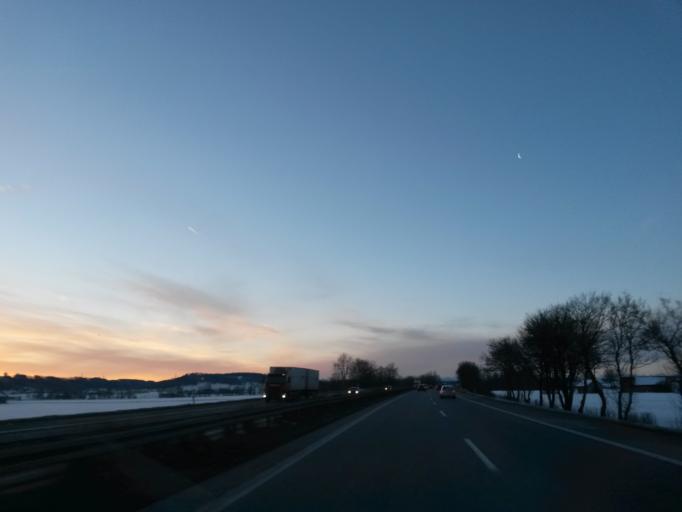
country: DE
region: Bavaria
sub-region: Swabia
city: Wolfertschwenden
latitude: 47.9035
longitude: 10.2420
